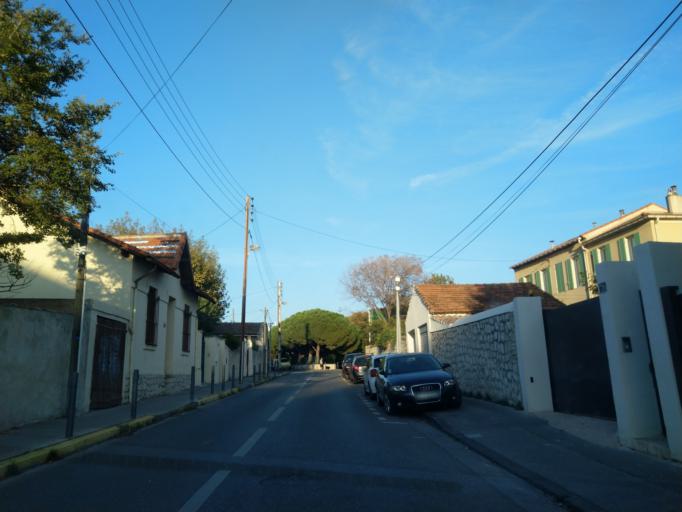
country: FR
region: Provence-Alpes-Cote d'Azur
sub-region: Departement des Bouches-du-Rhone
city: Marseille 08
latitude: 43.2466
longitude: 5.3787
